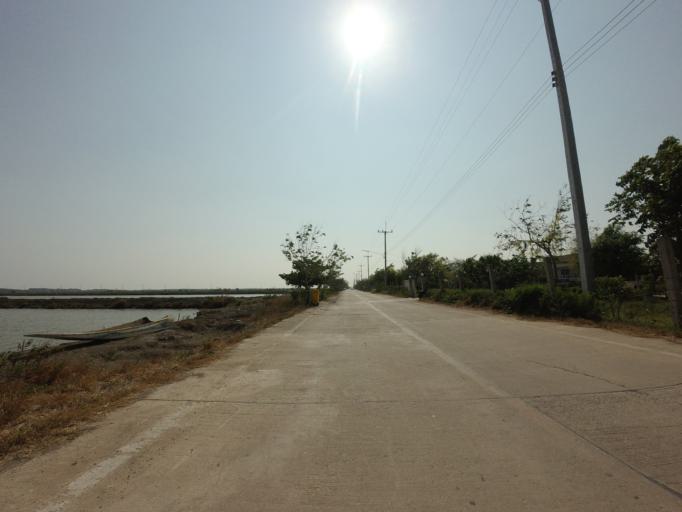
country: TH
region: Samut Sakhon
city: Samut Sakhon
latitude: 13.4991
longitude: 100.3597
